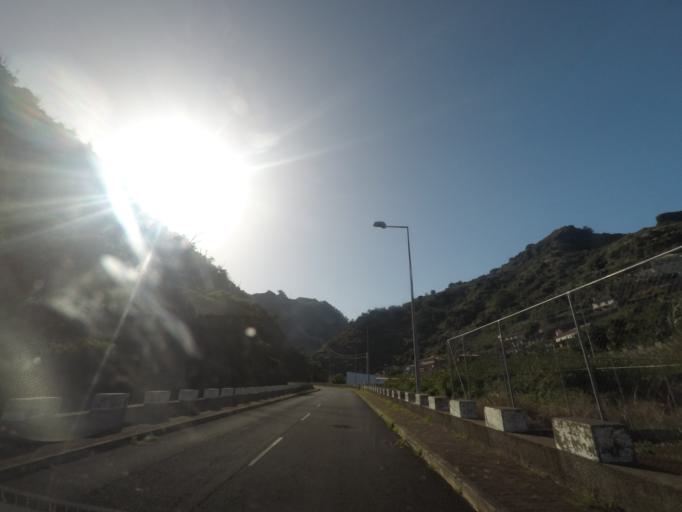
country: PT
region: Madeira
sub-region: Santa Cruz
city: Santa Cruz
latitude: 32.6914
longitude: -16.7995
